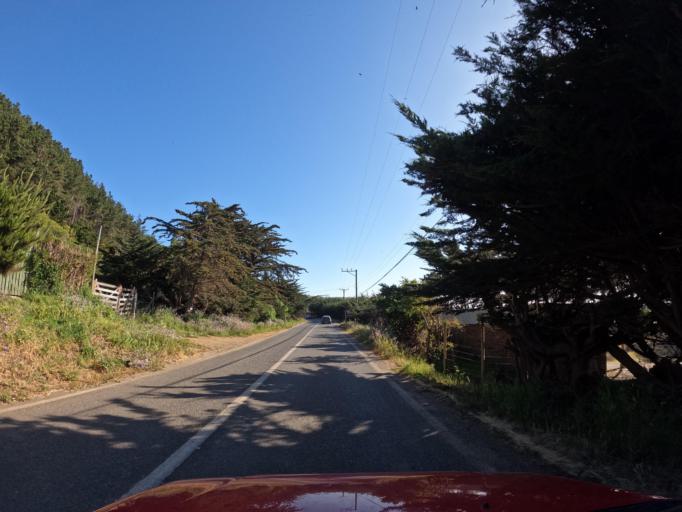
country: CL
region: Maule
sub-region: Provincia de Talca
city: Constitucion
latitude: -34.8770
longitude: -72.1547
